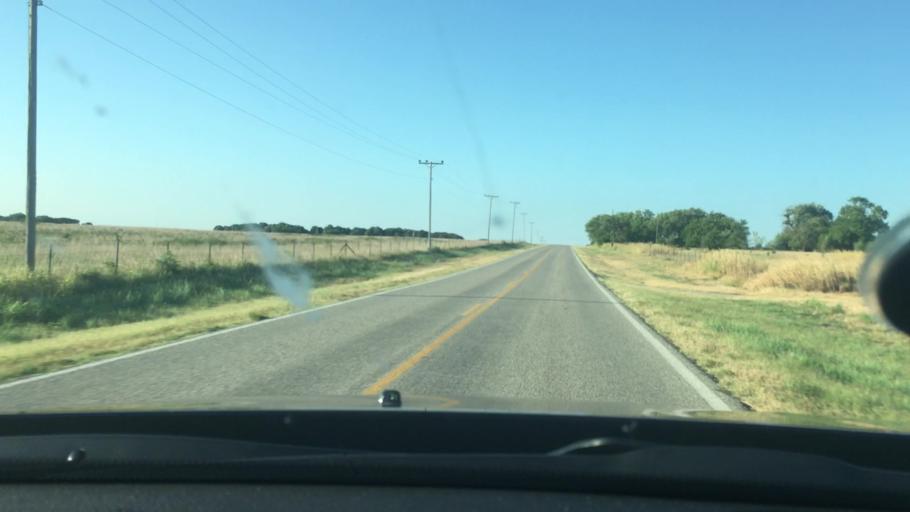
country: US
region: Oklahoma
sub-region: Murray County
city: Sulphur
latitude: 34.5756
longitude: -96.8448
